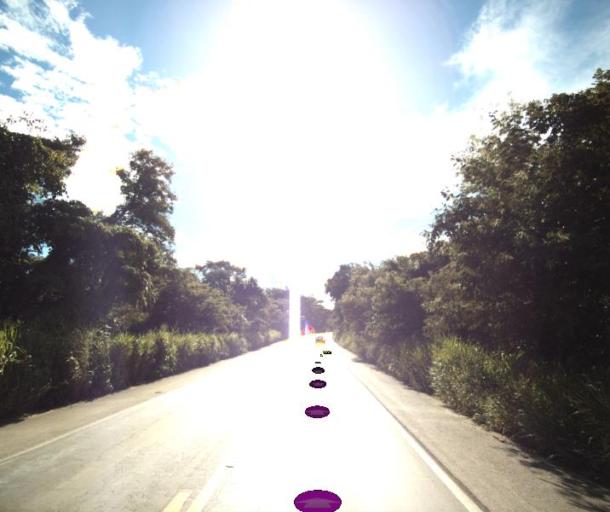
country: BR
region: Goias
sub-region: Uruana
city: Uruana
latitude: -15.5260
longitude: -49.4620
